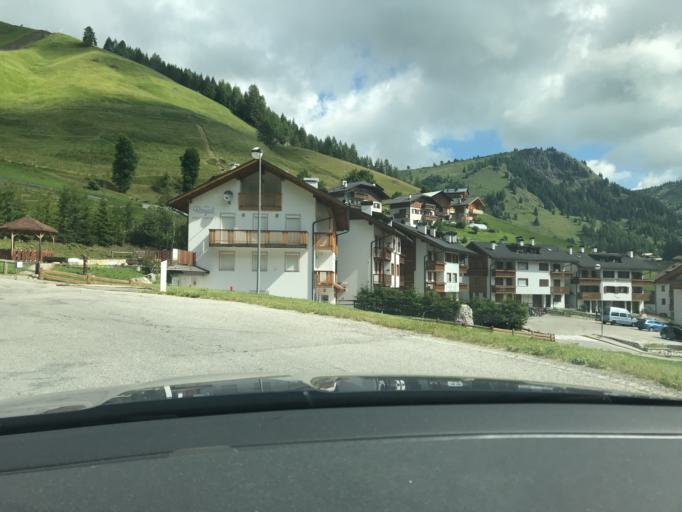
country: IT
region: Trentino-Alto Adige
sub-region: Bolzano
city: Corvara in Badia
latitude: 46.4946
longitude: 11.8671
